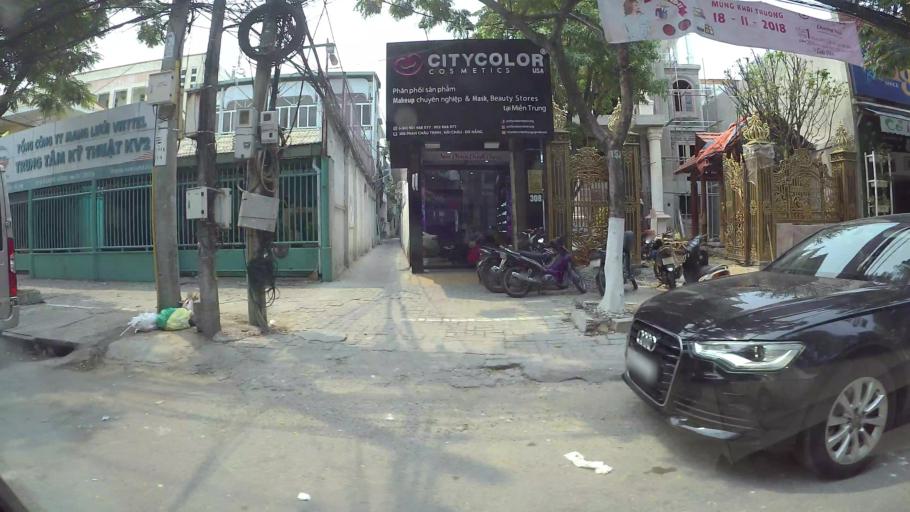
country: VN
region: Da Nang
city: Da Nang
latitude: 16.0580
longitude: 108.2190
